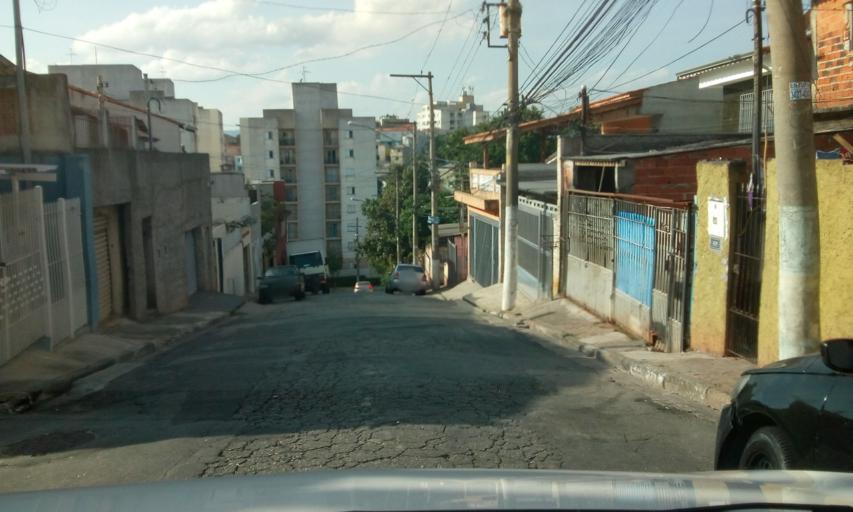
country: BR
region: Sao Paulo
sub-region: Sao Paulo
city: Sao Paulo
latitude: -23.4964
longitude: -46.6795
